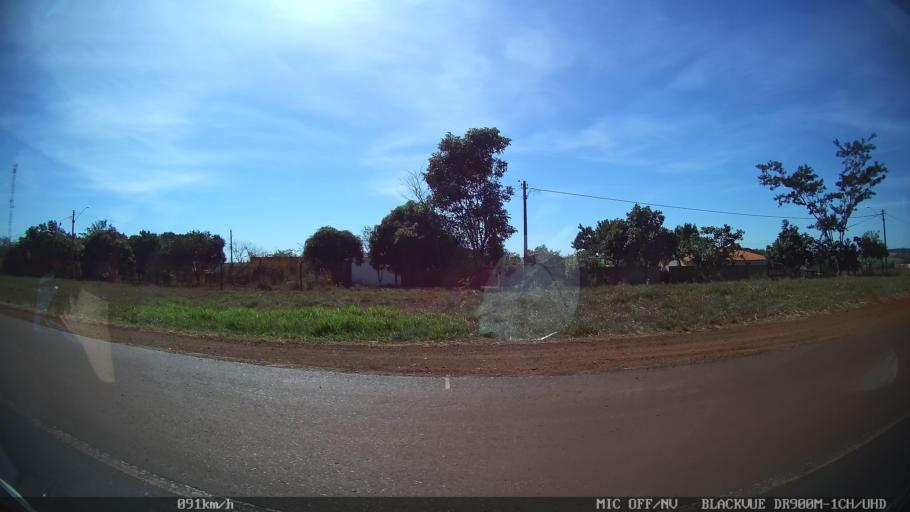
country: BR
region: Sao Paulo
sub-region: Sao Joaquim Da Barra
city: Sao Joaquim da Barra
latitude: -20.5226
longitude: -47.8443
